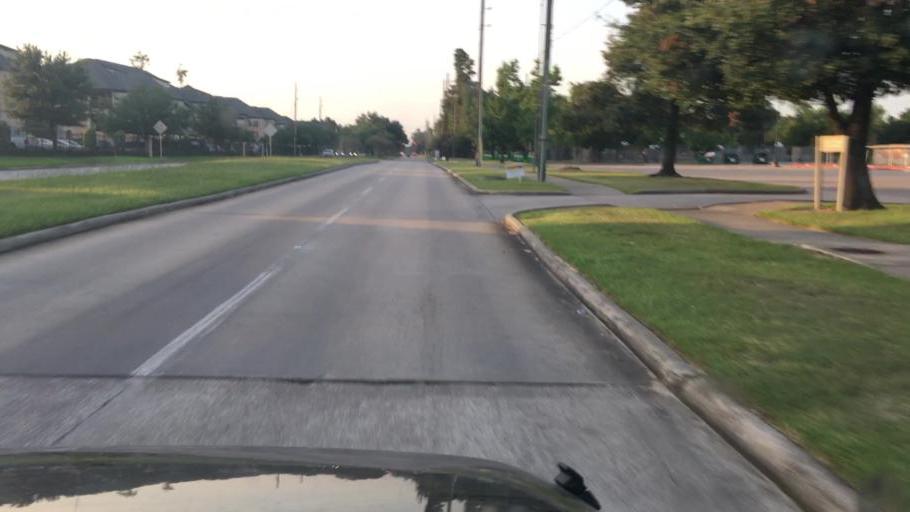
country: US
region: Texas
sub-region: Harris County
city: Atascocita
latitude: 29.9782
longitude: -95.2122
